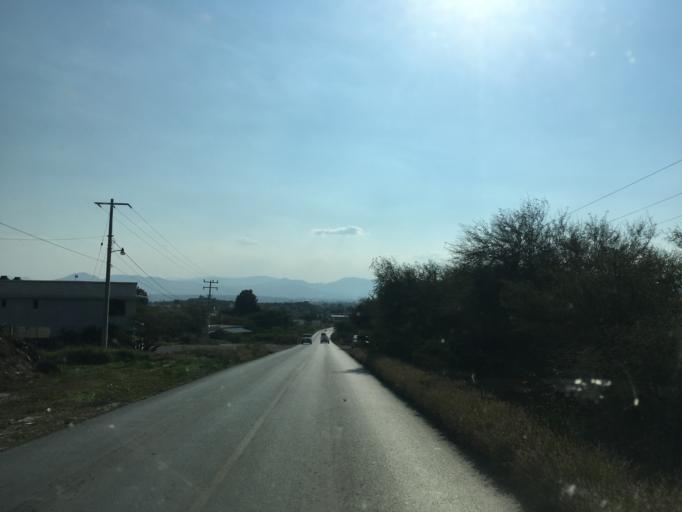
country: MX
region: Hidalgo
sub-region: Ixmiquilpan
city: El Nith
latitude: 20.5592
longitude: -99.1560
